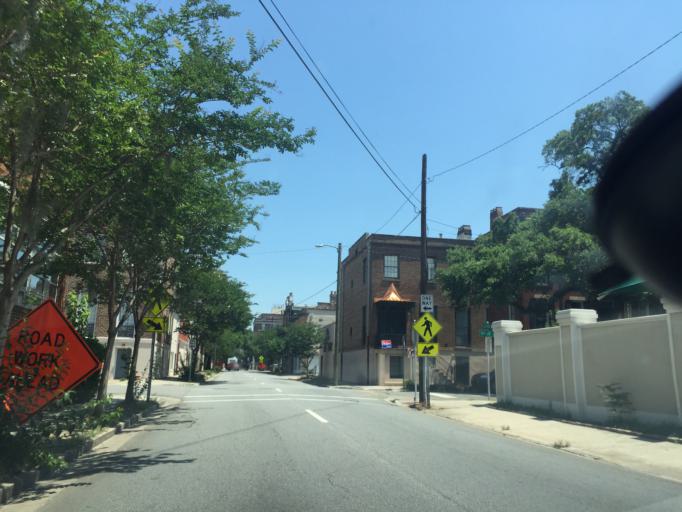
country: US
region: Georgia
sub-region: Chatham County
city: Savannah
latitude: 32.0711
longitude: -81.0936
